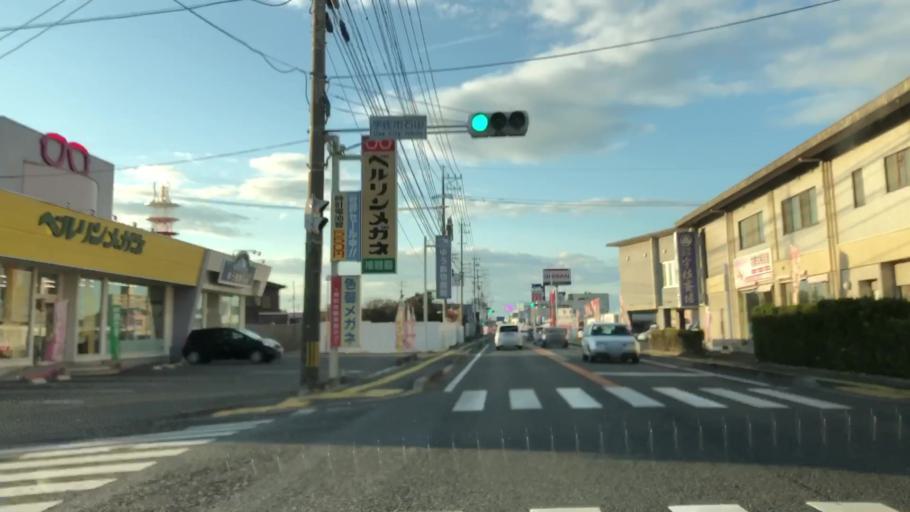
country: JP
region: Oita
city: Bungo-Takada-shi
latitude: 33.5323
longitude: 131.3327
